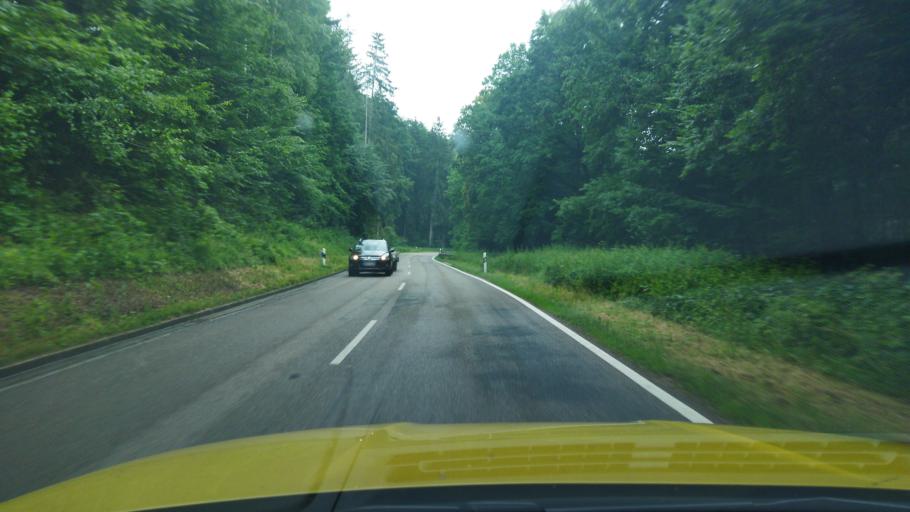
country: DE
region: Bavaria
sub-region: Regierungsbezirk Mittelfranken
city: Hottingen
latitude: 49.0862
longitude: 11.0080
